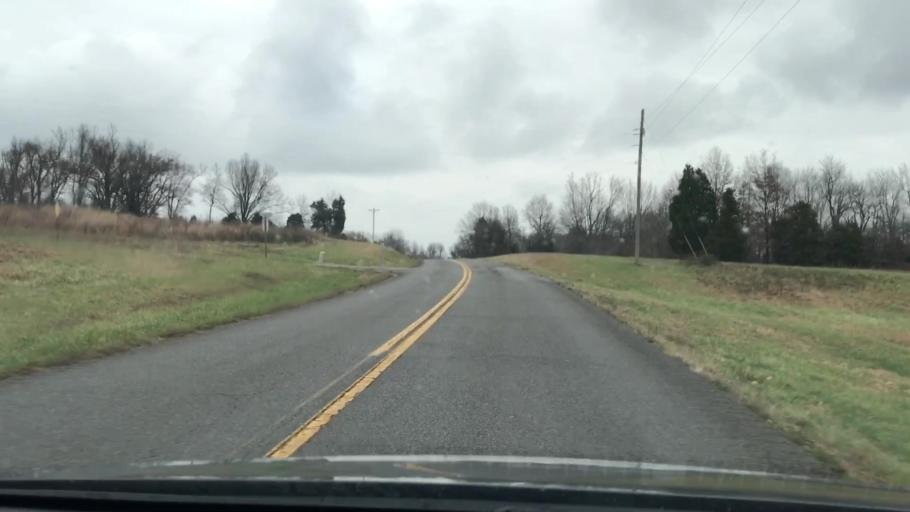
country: US
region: Kentucky
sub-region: Webster County
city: Sebree
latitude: 37.4992
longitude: -87.4379
